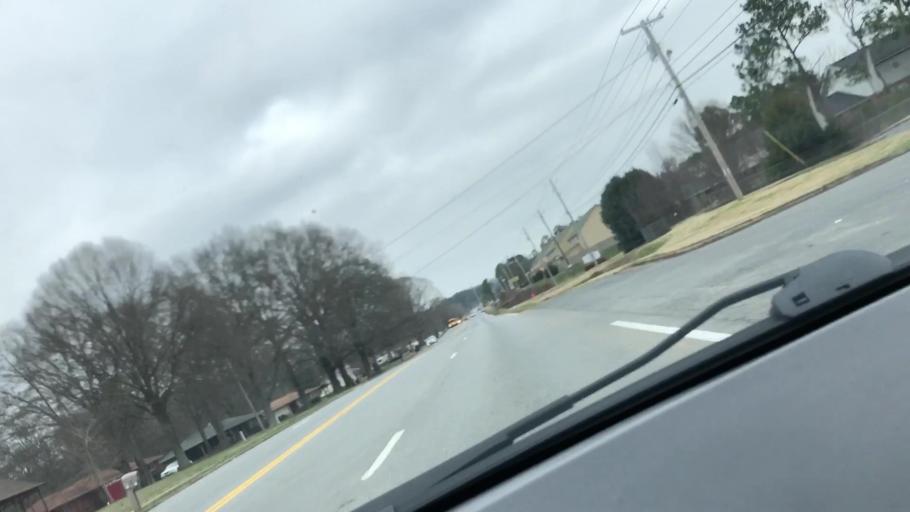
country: US
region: Georgia
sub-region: Bartow County
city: Cartersville
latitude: 34.2140
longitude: -84.8189
